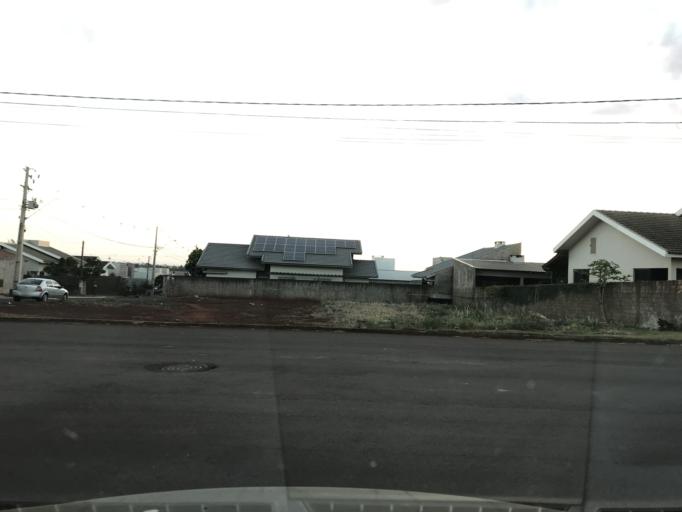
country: BR
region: Parana
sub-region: Palotina
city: Palotina
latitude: -24.3027
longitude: -53.8373
